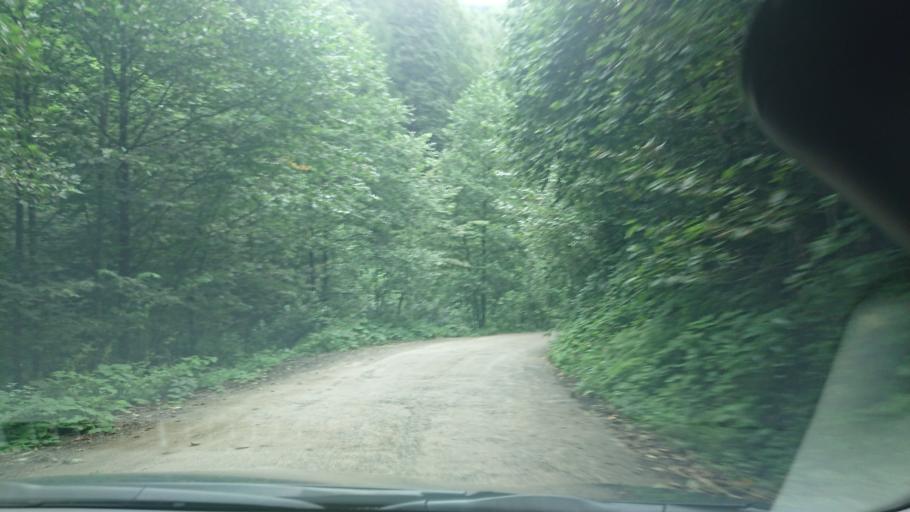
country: TR
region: Gumushane
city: Kurtun
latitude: 40.6686
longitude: 39.0389
